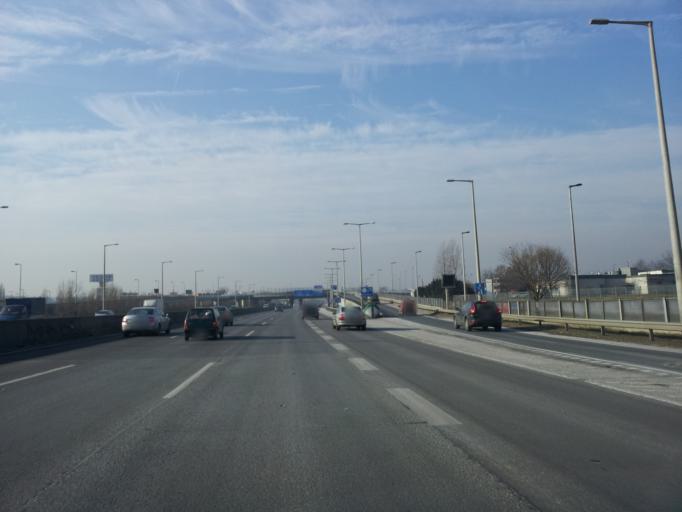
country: HU
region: Pest
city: Budaors
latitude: 47.4534
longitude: 18.9665
